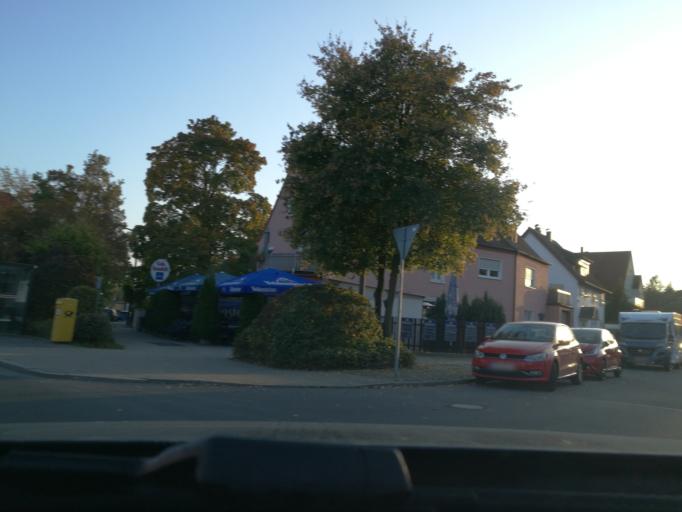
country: DE
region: Bavaria
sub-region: Regierungsbezirk Mittelfranken
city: Furth
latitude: 49.4905
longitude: 10.9951
